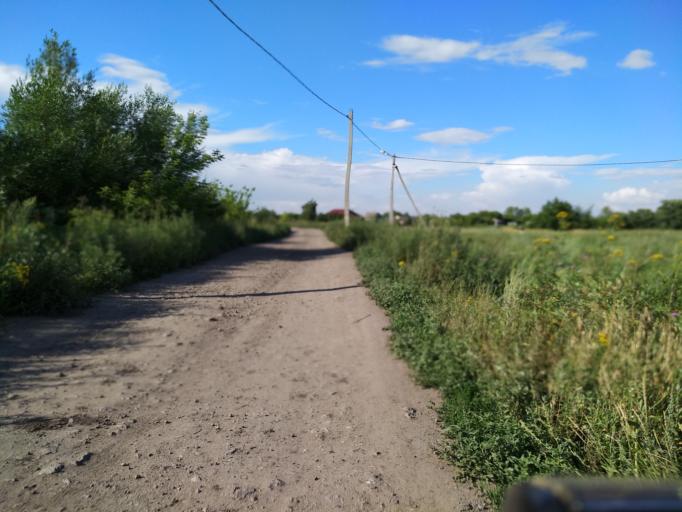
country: RU
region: Lipetsk
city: Dobrinka
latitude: 52.0317
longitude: 40.5628
